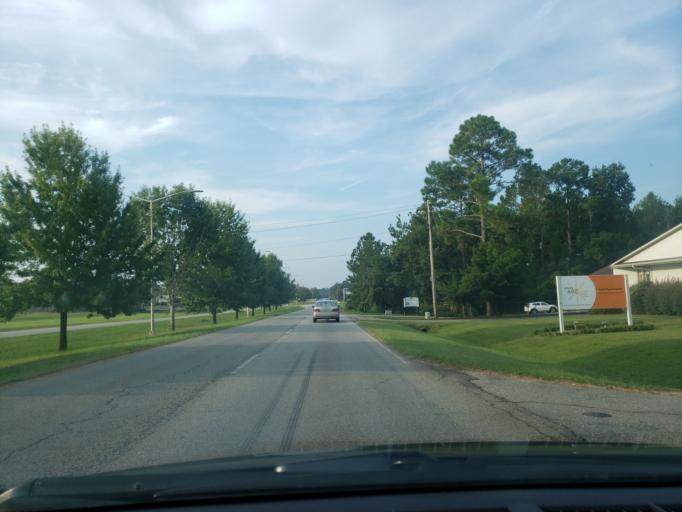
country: US
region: Georgia
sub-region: Dougherty County
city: Albany
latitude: 31.5896
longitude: -84.2196
